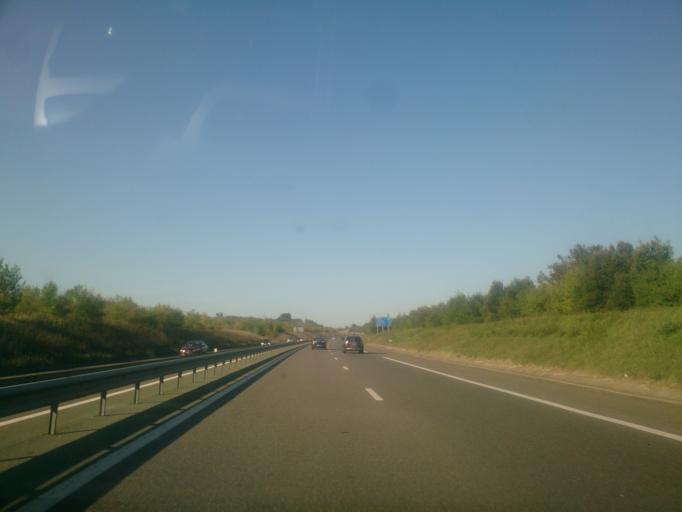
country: FR
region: Midi-Pyrenees
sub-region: Departement du Tarn-et-Garonne
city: Caussade
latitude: 44.1615
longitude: 1.5199
